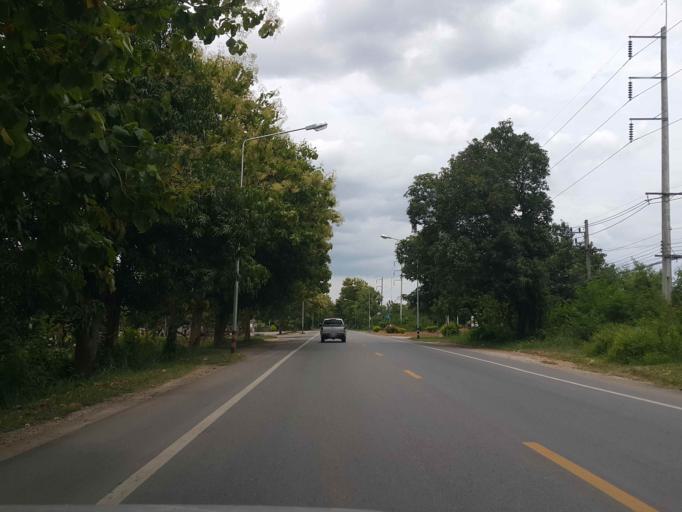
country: TH
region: Lamphun
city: Pa Sang
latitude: 18.4547
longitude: 98.9000
